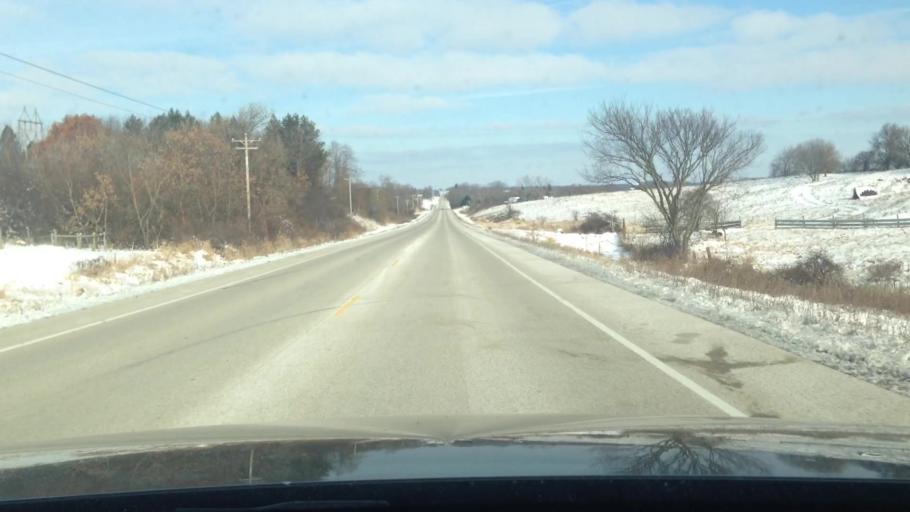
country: US
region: Wisconsin
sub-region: Walworth County
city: East Troy
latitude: 42.7009
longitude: -88.4050
